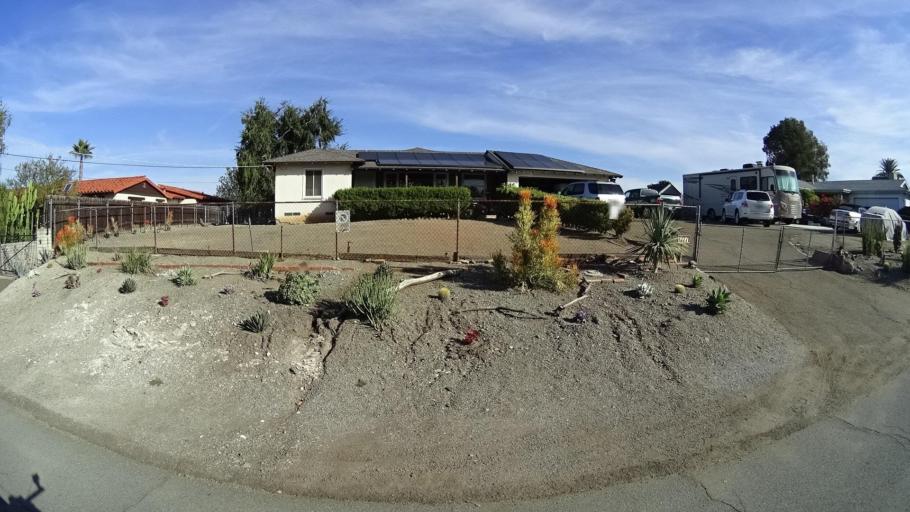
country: US
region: California
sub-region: San Diego County
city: Casa de Oro-Mount Helix
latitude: 32.7379
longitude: -116.9692
